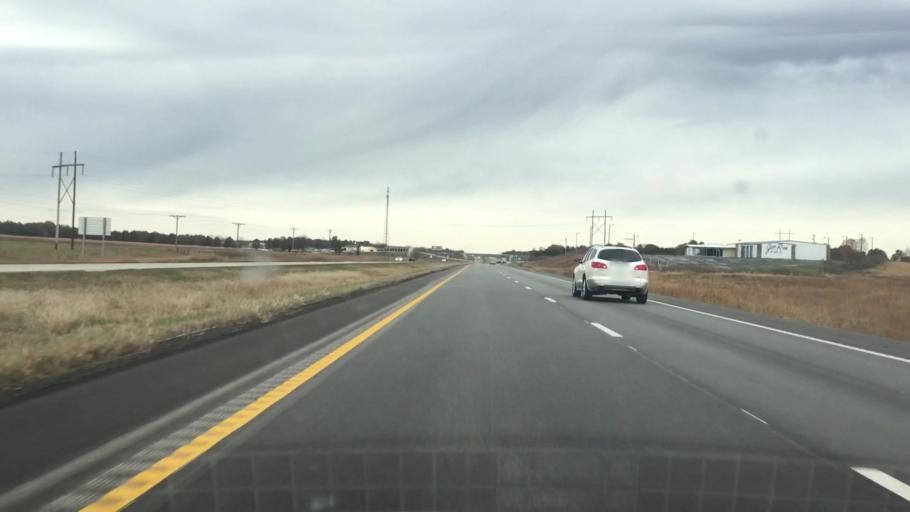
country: US
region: Missouri
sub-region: Saint Clair County
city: Osceola
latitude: 38.0300
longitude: -93.6756
